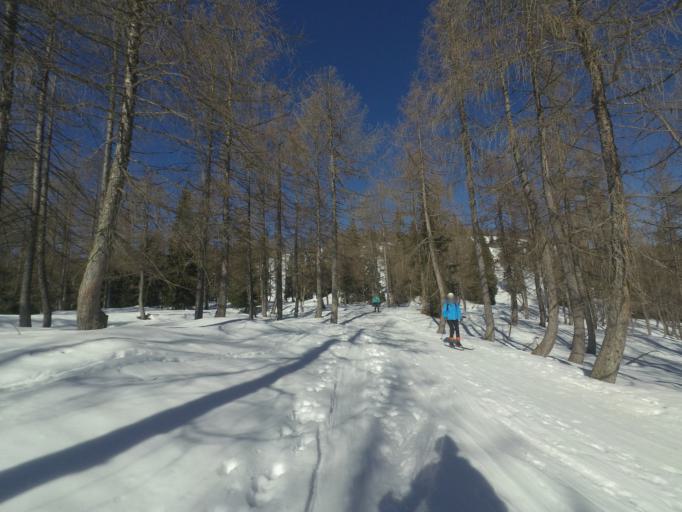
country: AT
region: Upper Austria
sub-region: Politischer Bezirk Gmunden
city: Sankt Wolfgang im Salzkammergut
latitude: 47.6565
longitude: 13.3937
